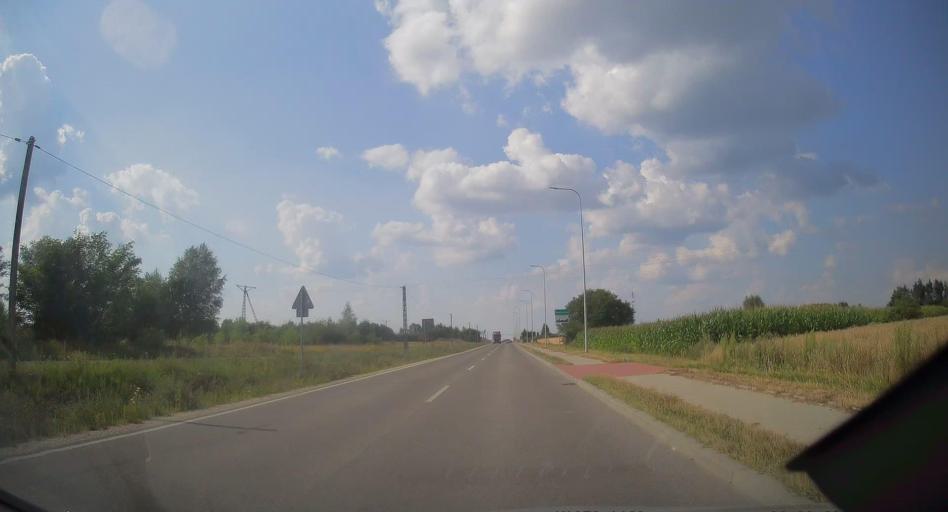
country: PL
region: Swietokrzyskie
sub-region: Powiat konecki
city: Radoszyce
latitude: 51.0661
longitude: 20.2719
